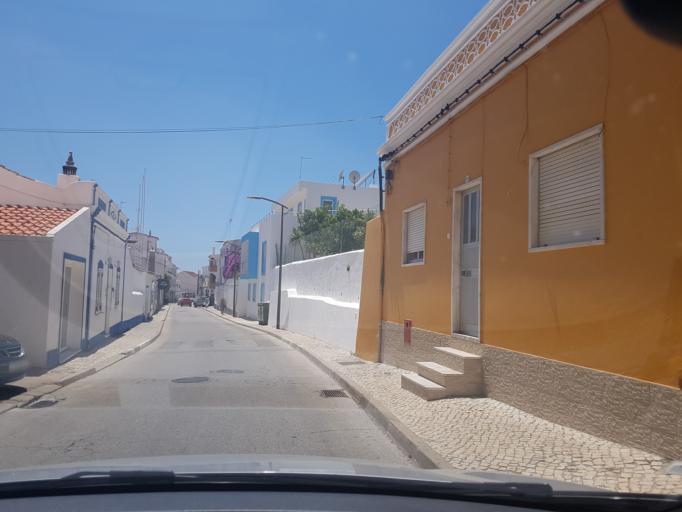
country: PT
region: Faro
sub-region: Lagoa
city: Carvoeiro
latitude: 37.1003
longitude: -8.4693
